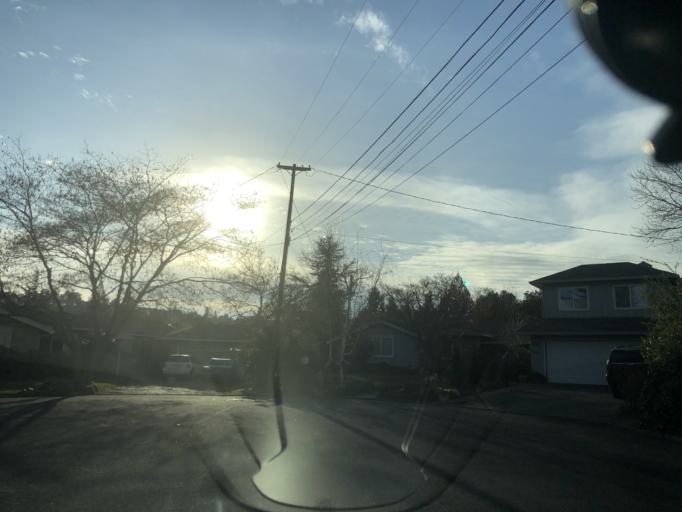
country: US
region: California
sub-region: Contra Costa County
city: Saranap
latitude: 37.8903
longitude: -122.0733
